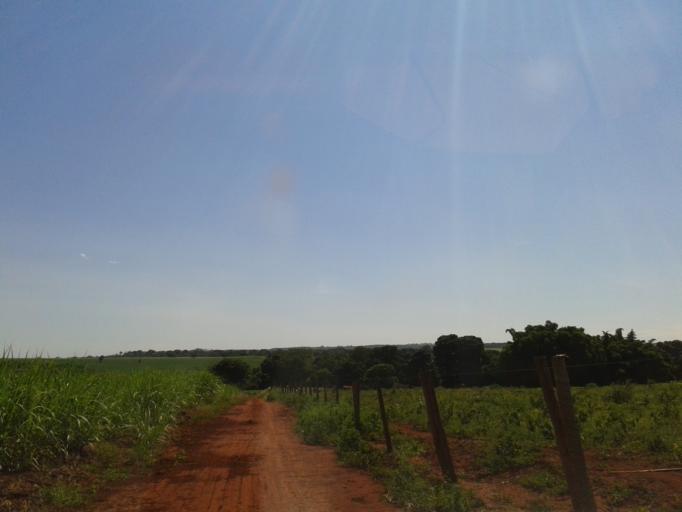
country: BR
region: Minas Gerais
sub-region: Centralina
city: Centralina
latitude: -18.6315
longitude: -49.2503
